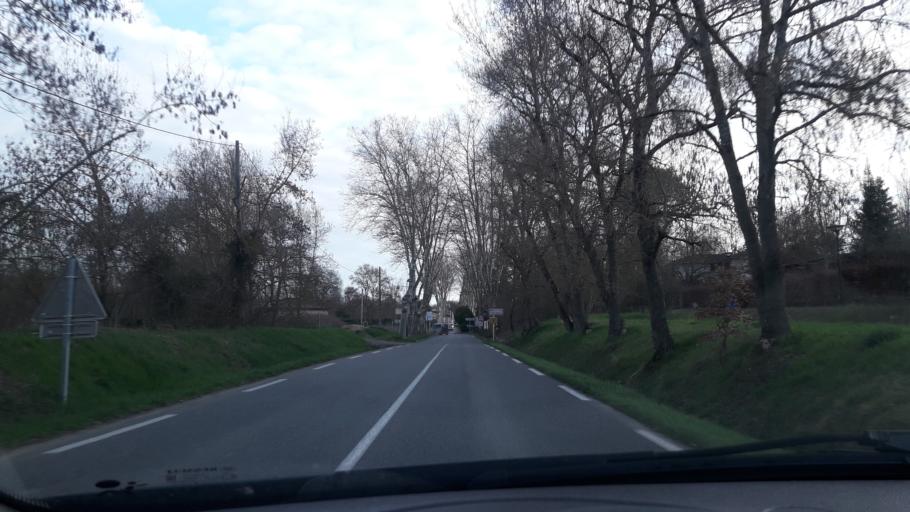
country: FR
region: Midi-Pyrenees
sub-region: Departement de la Haute-Garonne
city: Montaigut-sur-Save
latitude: 43.6893
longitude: 1.2281
